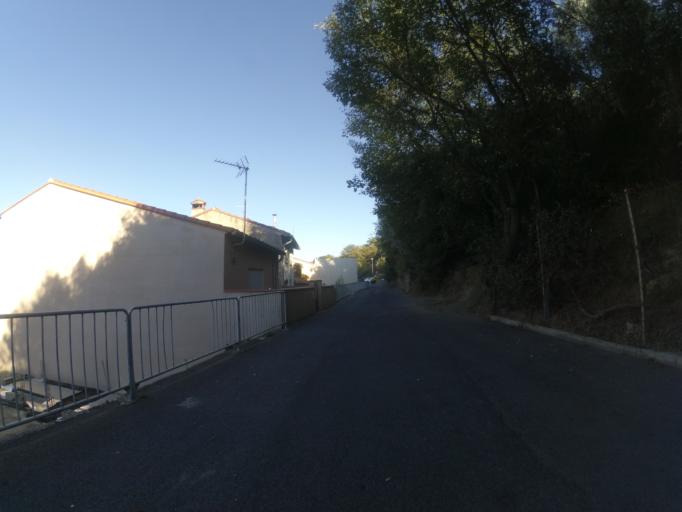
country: FR
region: Languedoc-Roussillon
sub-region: Departement des Pyrenees-Orientales
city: Corneilla-la-Riviere
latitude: 42.6816
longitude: 2.7414
